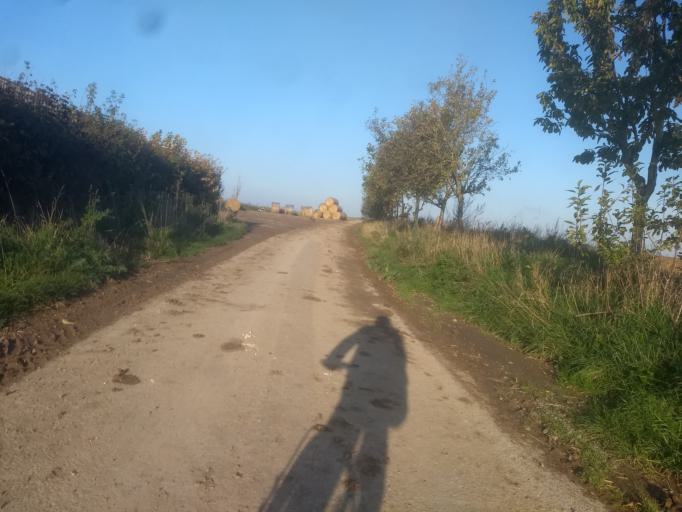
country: FR
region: Nord-Pas-de-Calais
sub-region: Departement du Pas-de-Calais
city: Tilloy-les-Mofflaines
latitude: 50.2798
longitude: 2.8204
